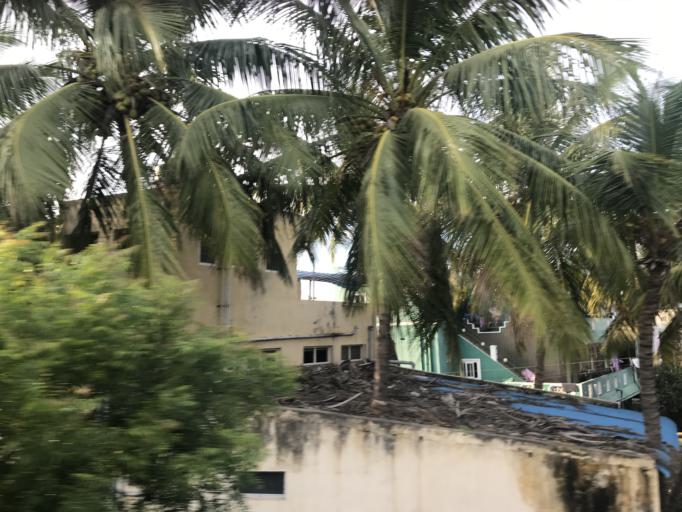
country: IN
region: Tamil Nadu
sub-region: Coimbatore
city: Coimbatore
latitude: 11.0307
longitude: 76.9568
